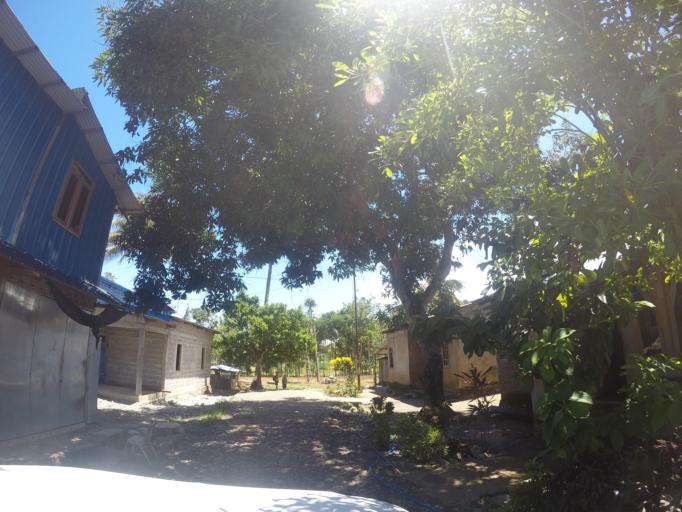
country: TL
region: Bobonaro
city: Maliana
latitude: -8.9713
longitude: 125.2168
